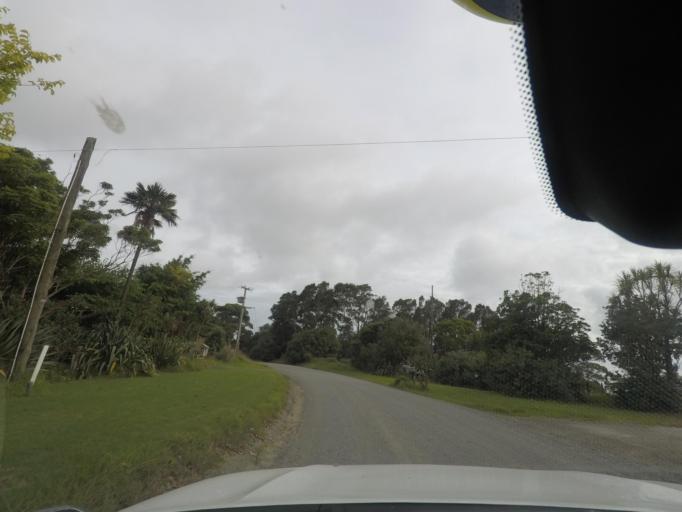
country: NZ
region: Auckland
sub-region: Auckland
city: Parakai
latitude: -36.4759
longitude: 174.2576
